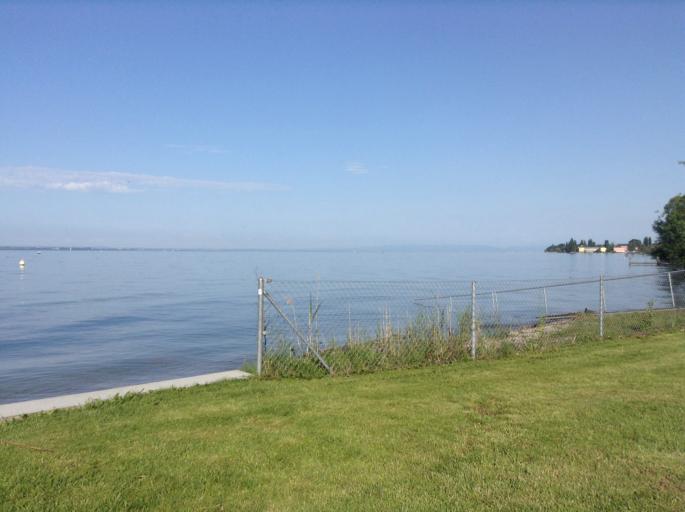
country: CH
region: Thurgau
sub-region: Kreuzlingen District
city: Bottighofen
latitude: 47.6419
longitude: 9.2141
